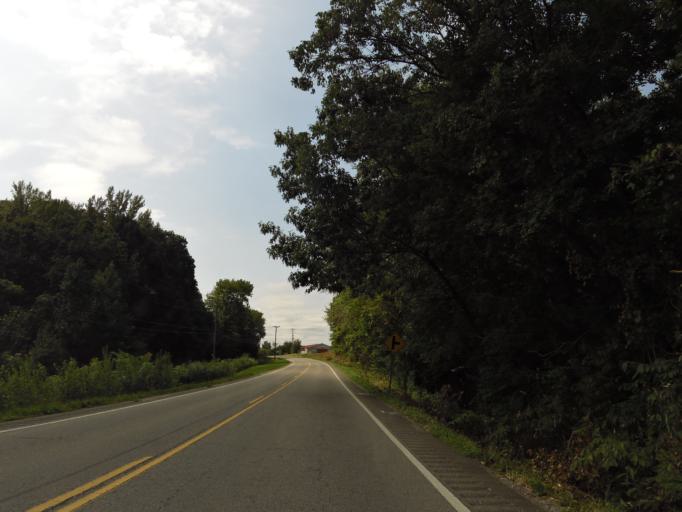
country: US
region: Tennessee
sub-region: Humphreys County
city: Waverly
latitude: 35.8687
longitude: -87.8084
